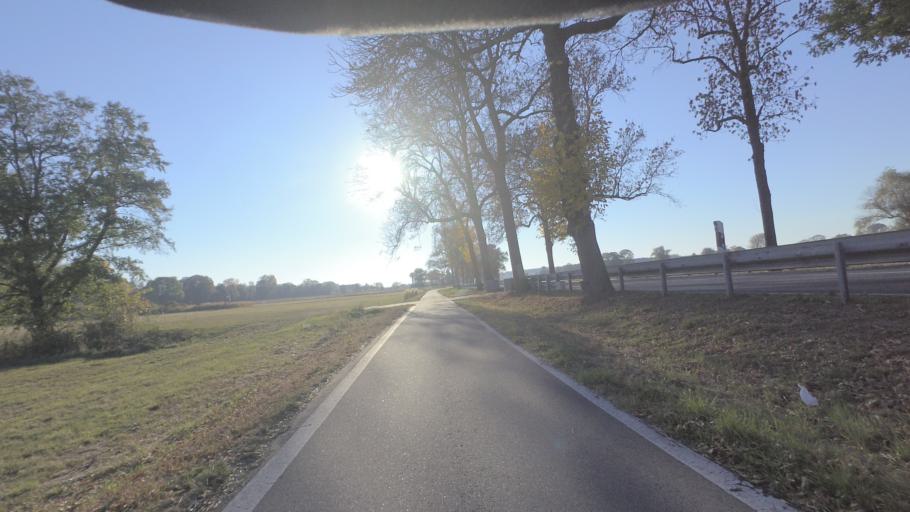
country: DE
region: Brandenburg
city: Mittenwalde
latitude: 52.2564
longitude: 13.5294
